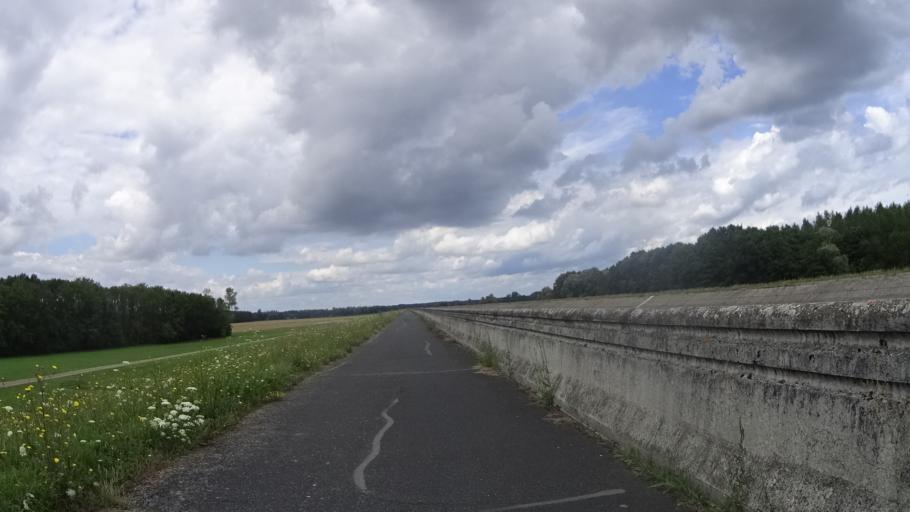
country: FR
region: Champagne-Ardenne
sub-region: Departement de la Haute-Marne
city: Villiers-en-Lieu
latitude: 48.5794
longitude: 4.8508
